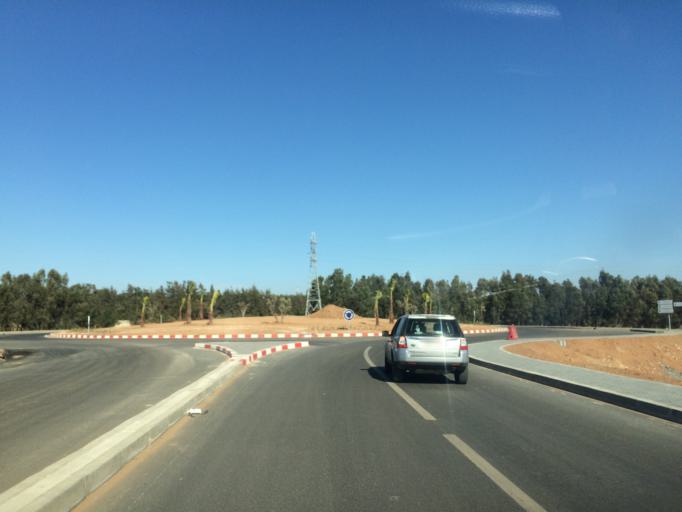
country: MA
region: Rabat-Sale-Zemmour-Zaer
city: Sale
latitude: 33.9776
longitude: -6.7360
